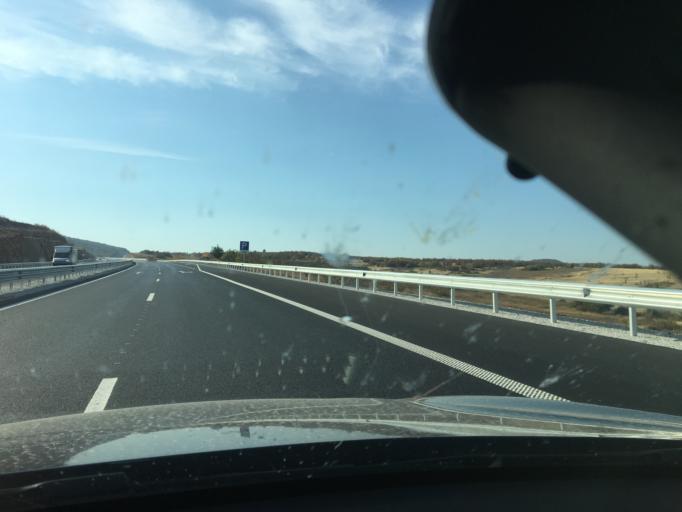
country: BG
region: Lovech
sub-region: Obshtina Yablanitsa
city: Yablanitsa
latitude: 43.0536
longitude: 24.2011
